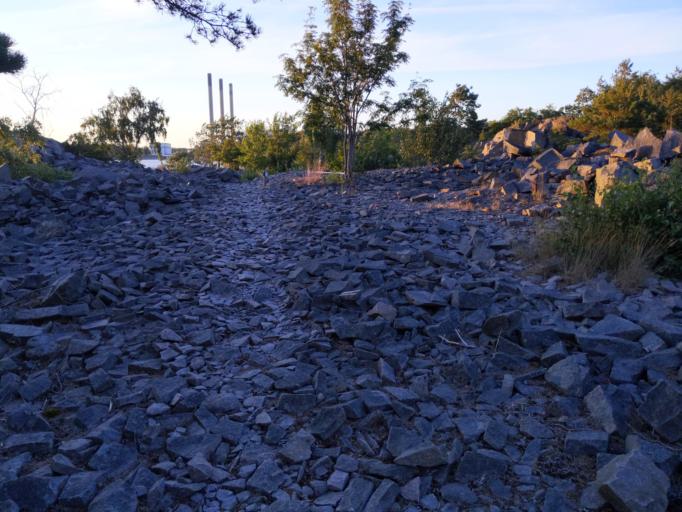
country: SE
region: Blekinge
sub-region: Karlshamns Kommun
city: Karlshamn
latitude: 56.1432
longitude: 14.8329
